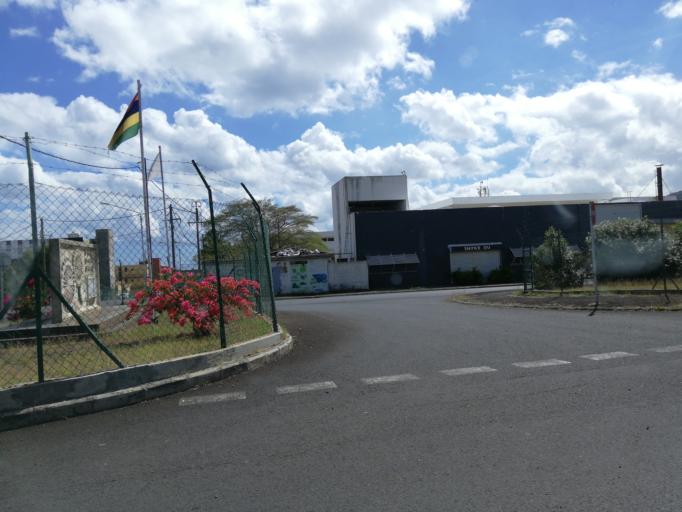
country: MU
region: Moka
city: Pailles
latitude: -20.1891
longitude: 57.4688
